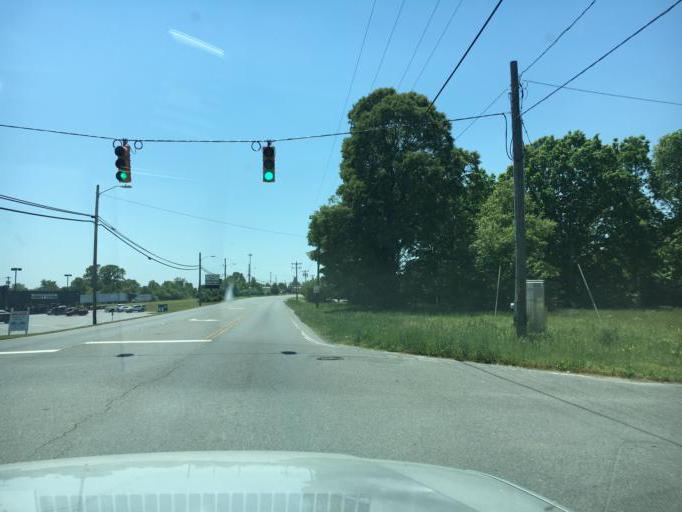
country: US
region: North Carolina
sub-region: Cleveland County
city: Shelby
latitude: 35.2678
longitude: -81.5540
